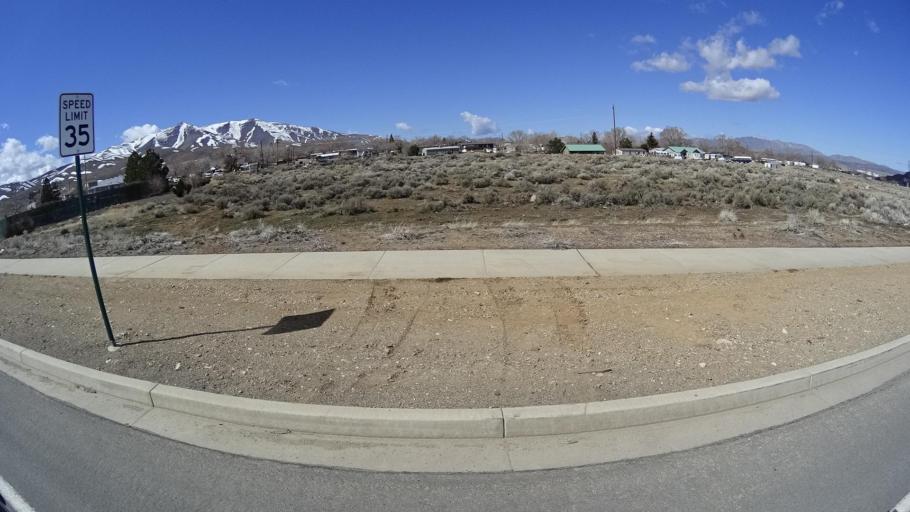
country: US
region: Nevada
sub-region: Washoe County
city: Golden Valley
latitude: 39.6077
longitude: -119.8522
